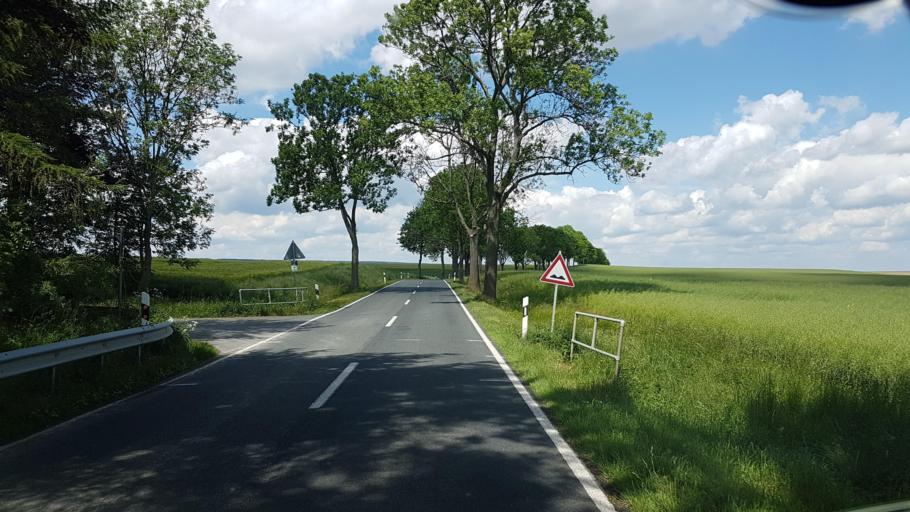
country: DE
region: Lower Saxony
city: Rabke
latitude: 52.1835
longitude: 10.8930
